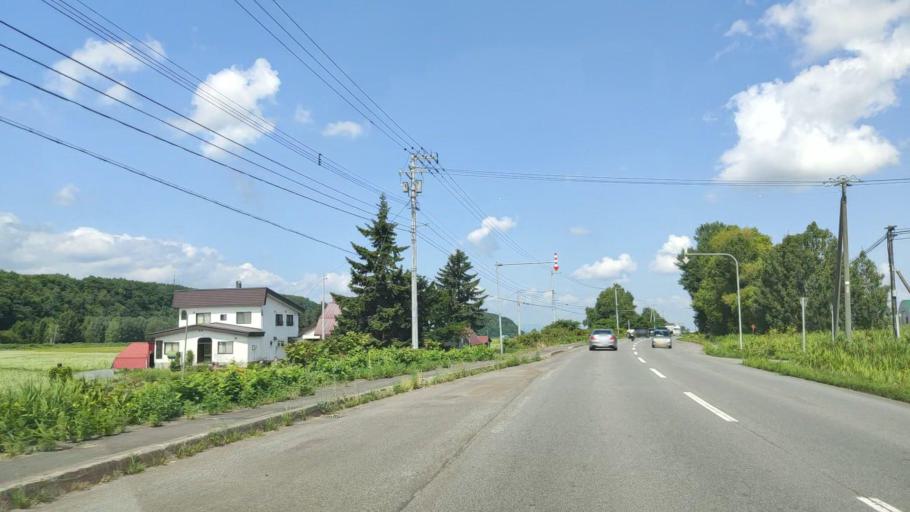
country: JP
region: Hokkaido
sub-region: Asahikawa-shi
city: Asahikawa
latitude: 43.6324
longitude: 142.4585
